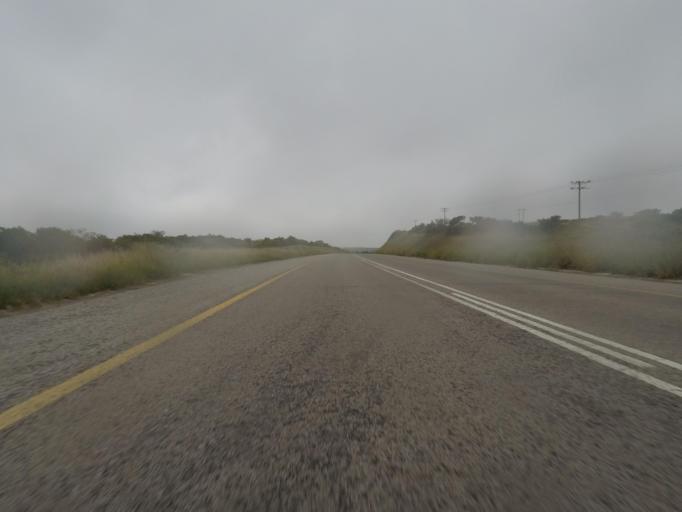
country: ZA
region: Eastern Cape
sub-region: Cacadu District Municipality
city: Grahamstown
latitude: -33.6423
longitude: 26.3683
